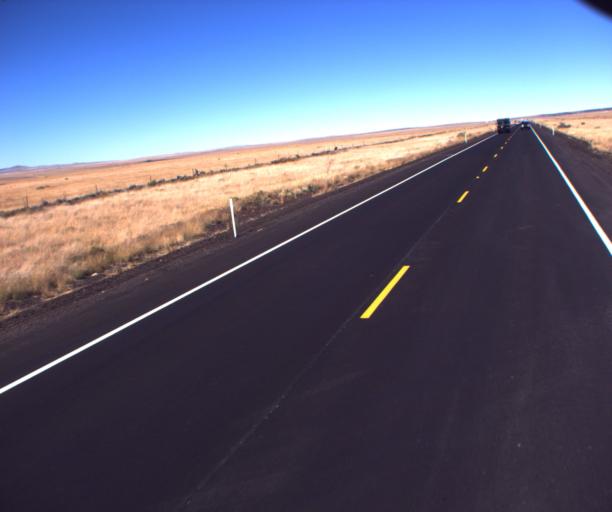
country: US
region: Arizona
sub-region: Apache County
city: Springerville
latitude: 34.2604
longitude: -109.3562
